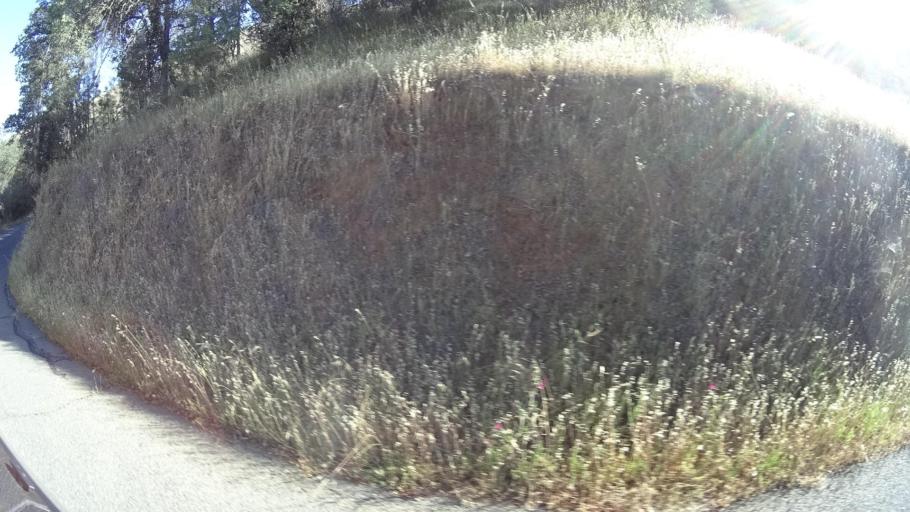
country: US
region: California
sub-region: Lake County
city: Nice
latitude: 39.1219
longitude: -122.8361
